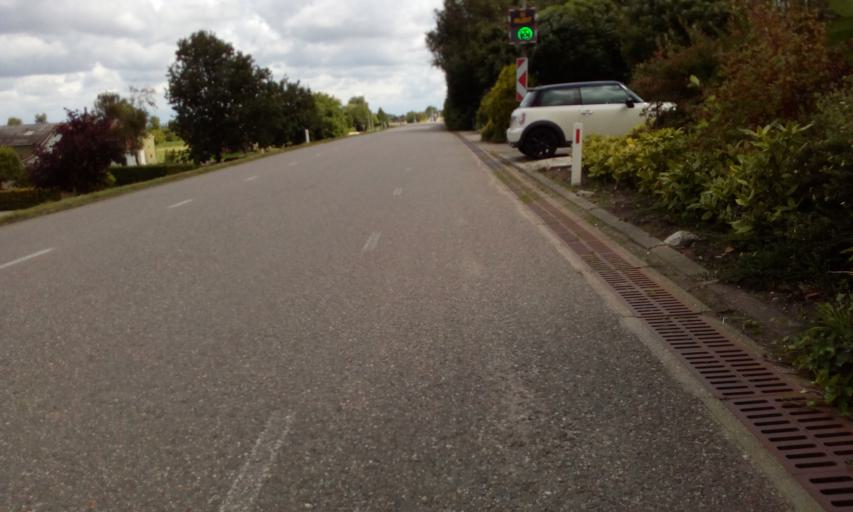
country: NL
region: South Holland
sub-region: Gemeente Barendrecht
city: Barendrecht
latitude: 51.8348
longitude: 4.5322
